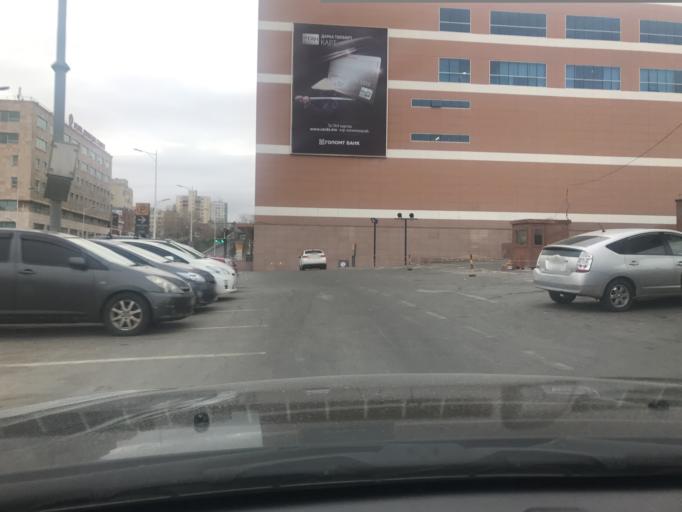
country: MN
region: Ulaanbaatar
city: Ulaanbaatar
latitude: 47.9231
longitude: 106.9325
